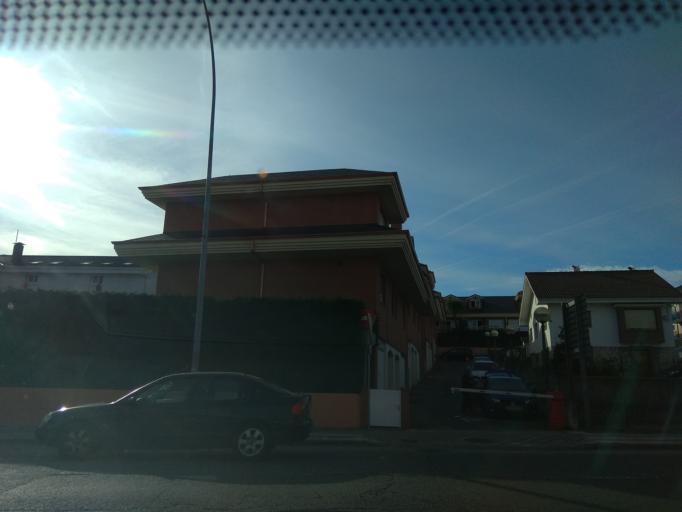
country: ES
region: Cantabria
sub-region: Provincia de Cantabria
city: El Astillero
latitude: 43.4208
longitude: -3.8472
